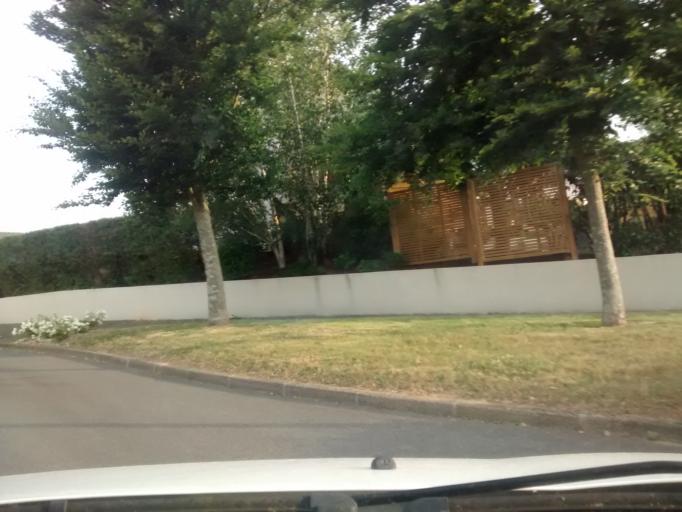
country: FR
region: Brittany
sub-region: Departement d'Ille-et-Vilaine
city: Cesson-Sevigne
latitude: 48.1257
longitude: -1.6165
